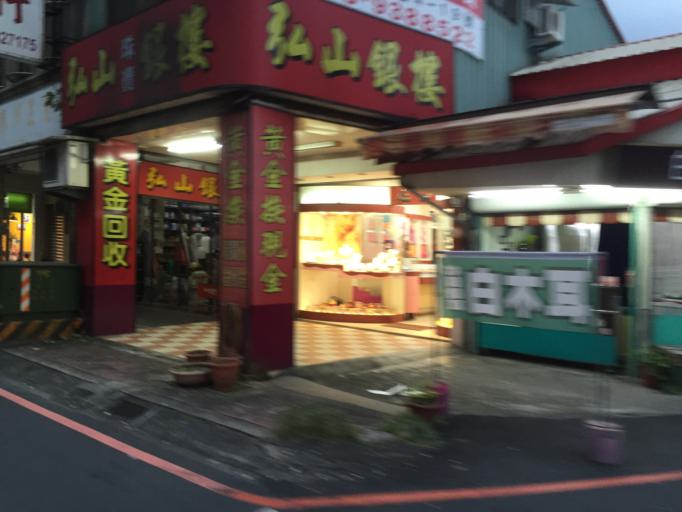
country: TW
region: Taiwan
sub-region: Yilan
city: Yilan
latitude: 24.7590
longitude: 121.7529
